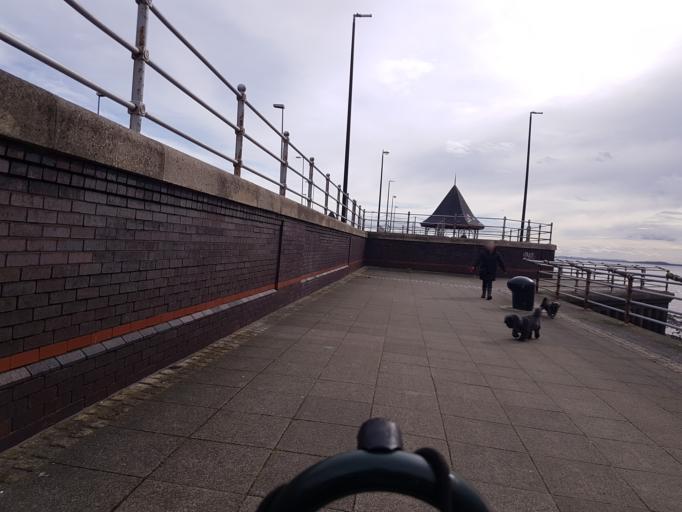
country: GB
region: England
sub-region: Metropolitan Borough of Wirral
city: Bromborough
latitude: 53.3749
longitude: -2.9661
